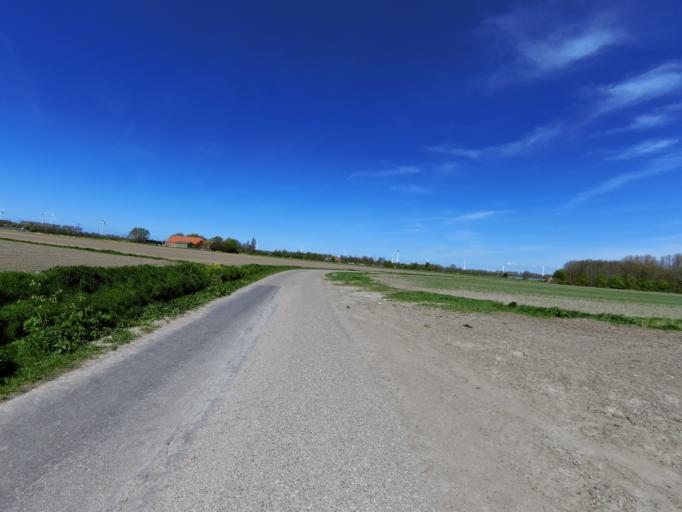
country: NL
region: South Holland
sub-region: Gemeente Brielle
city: Brielle
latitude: 51.9137
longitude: 4.1409
